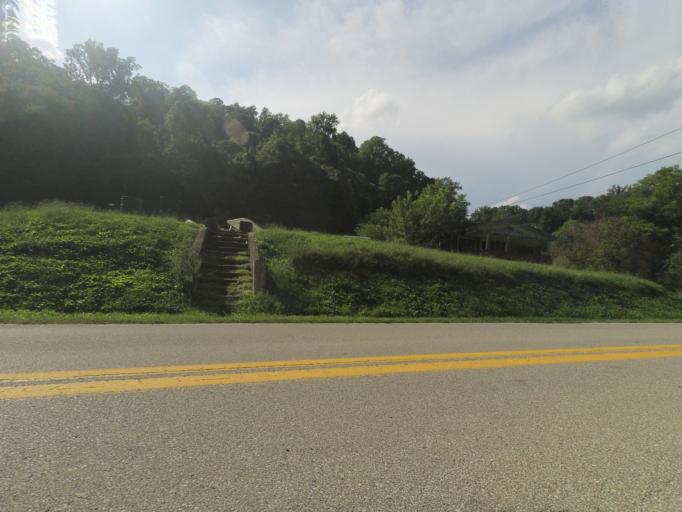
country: US
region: West Virginia
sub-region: Wayne County
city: Ceredo
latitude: 38.3848
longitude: -82.5615
